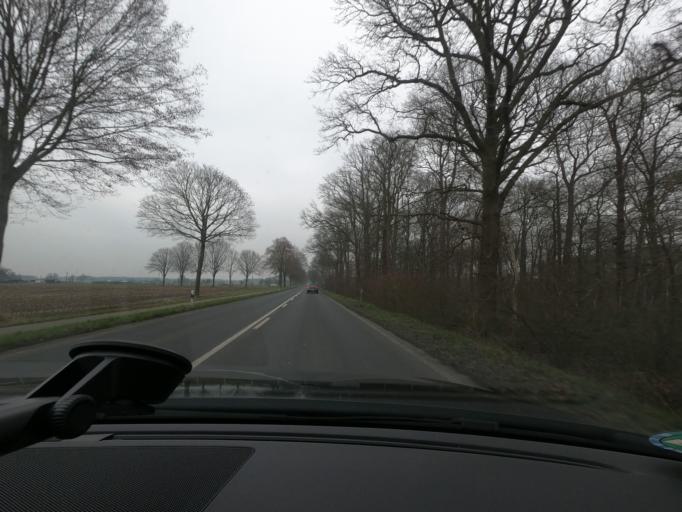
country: DE
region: North Rhine-Westphalia
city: Straelen
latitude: 51.3896
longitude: 6.2708
